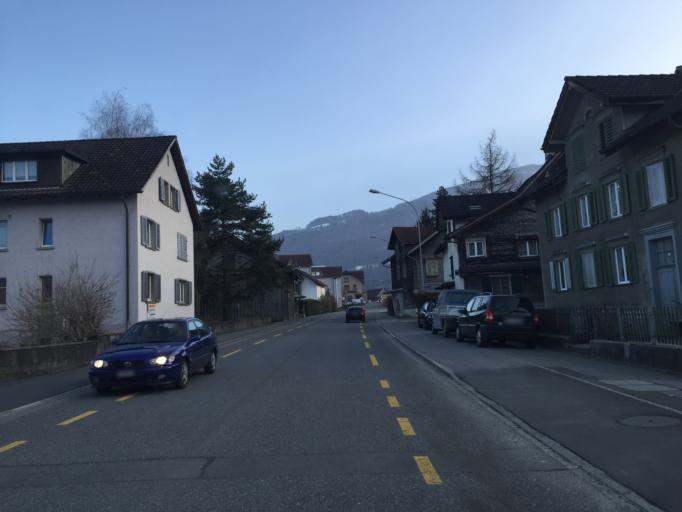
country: CH
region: Saint Gallen
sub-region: Wahlkreis Werdenberg
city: Grabs
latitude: 47.1855
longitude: 9.4428
